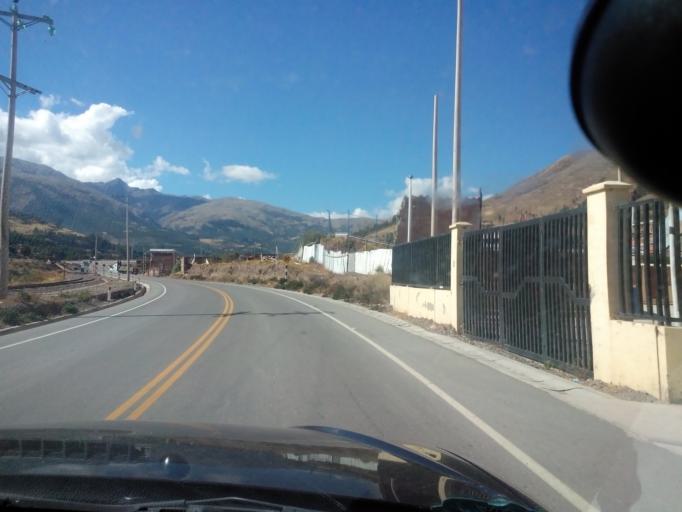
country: PE
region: Cusco
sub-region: Provincia de Quispicanchis
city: Urcos
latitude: -13.6832
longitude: -71.6248
